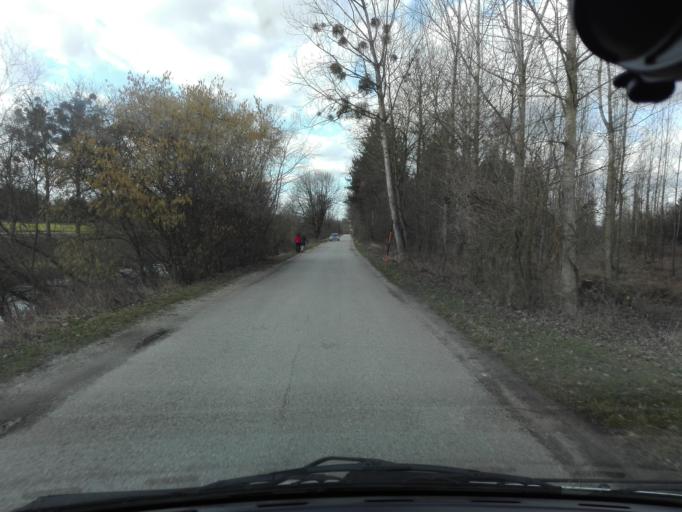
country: AT
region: Upper Austria
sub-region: Politischer Bezirk Perg
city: Perg
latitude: 48.2261
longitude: 14.6570
